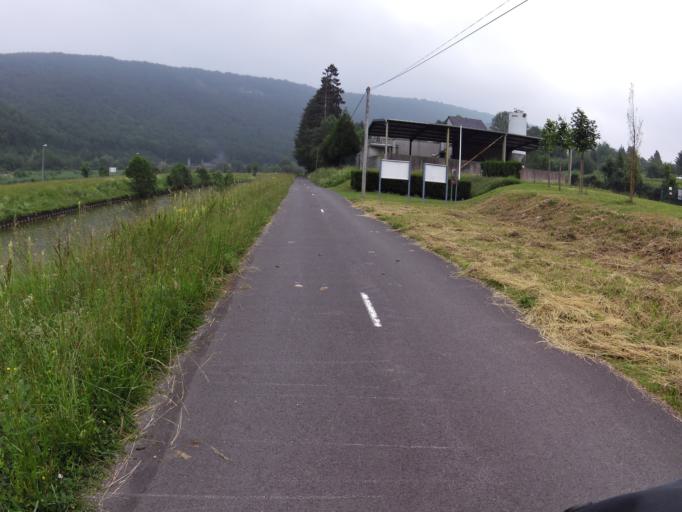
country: FR
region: Champagne-Ardenne
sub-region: Departement des Ardennes
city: Haybes
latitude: 50.0023
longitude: 4.6956
